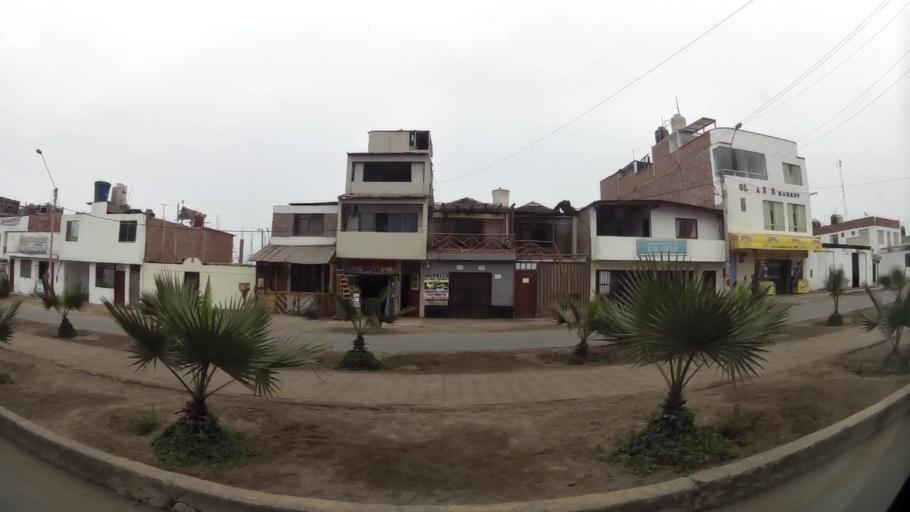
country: PE
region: Lima
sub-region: Lima
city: Punta Hermosa
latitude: -12.3316
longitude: -76.8248
